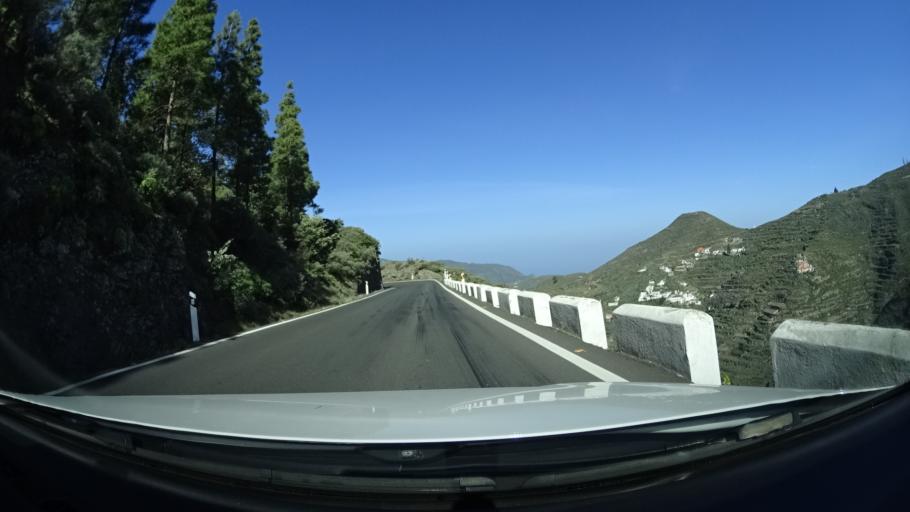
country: ES
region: Canary Islands
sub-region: Provincia de Las Palmas
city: Artenara
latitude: 28.0249
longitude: -15.6276
